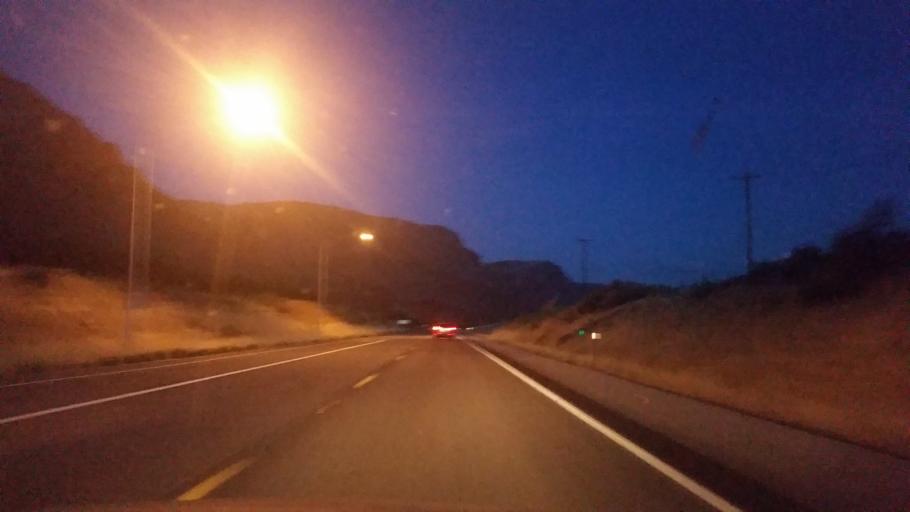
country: US
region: Washington
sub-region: Chelan County
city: South Wenatchee
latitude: 47.3643
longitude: -120.1198
